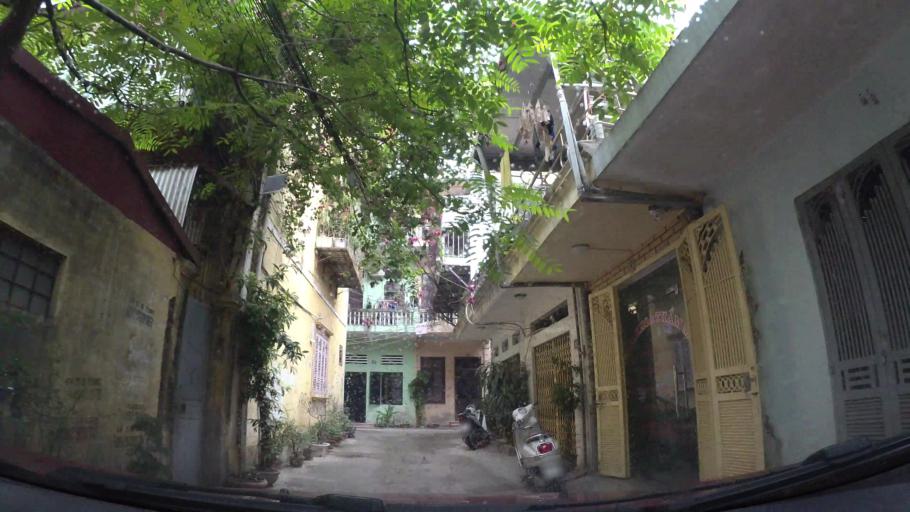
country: VN
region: Ha Noi
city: Dong Da
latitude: 21.0106
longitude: 105.8272
